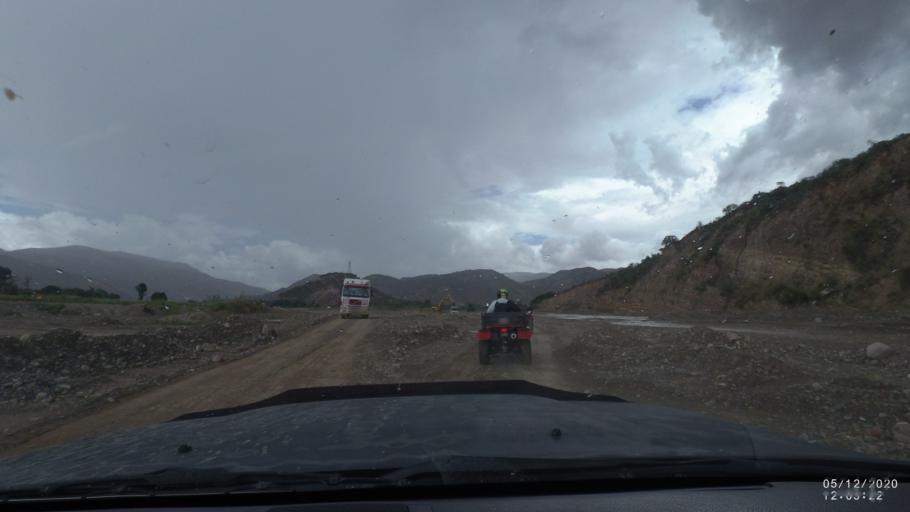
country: BO
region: Cochabamba
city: Sipe Sipe
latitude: -17.5724
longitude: -66.3519
